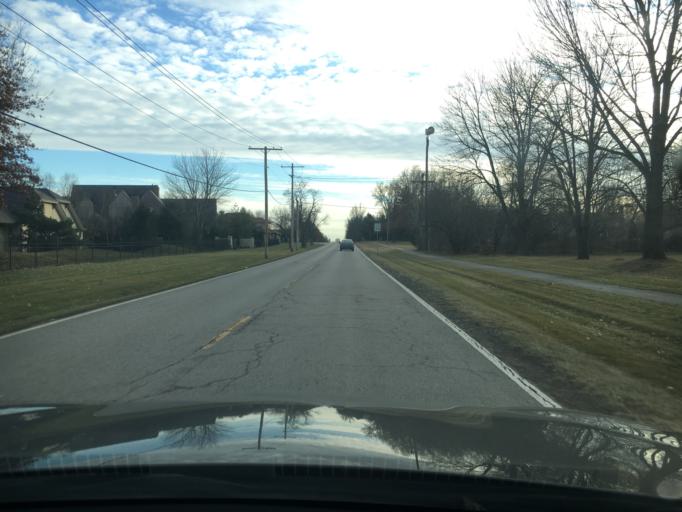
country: US
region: Kansas
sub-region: Johnson County
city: Leawood
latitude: 38.8774
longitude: -94.6306
